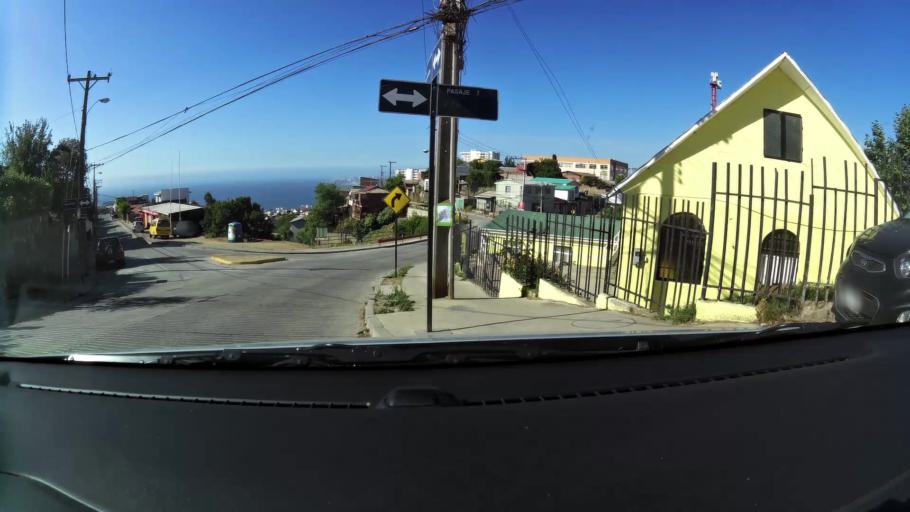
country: CL
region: Valparaiso
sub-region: Provincia de Valparaiso
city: Vina del Mar
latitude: -33.0449
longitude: -71.5588
